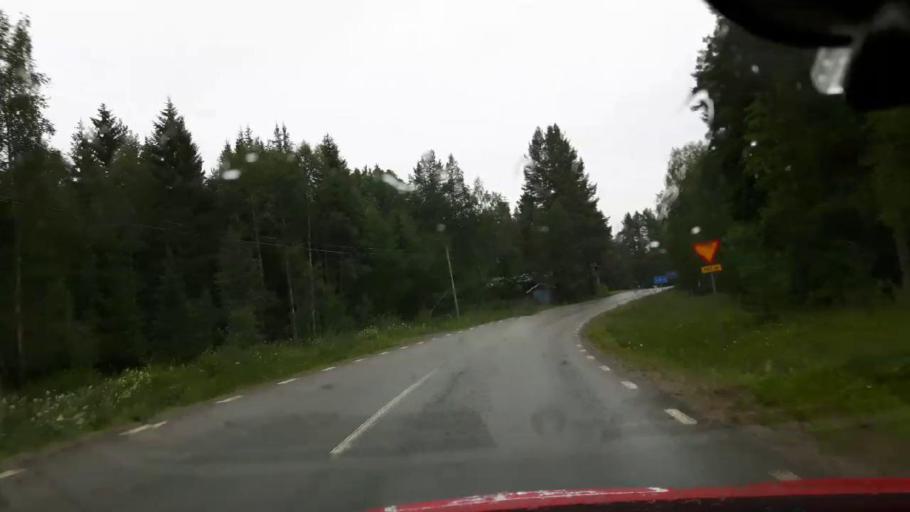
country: SE
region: Jaemtland
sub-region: OEstersunds Kommun
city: Brunflo
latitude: 62.7751
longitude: 15.0136
